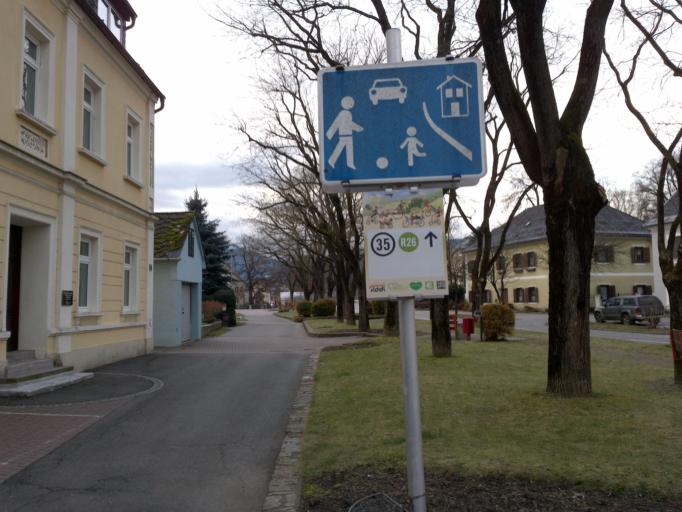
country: AT
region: Styria
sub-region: Politischer Bezirk Murtal
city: Weisskirchen in Steiermark
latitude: 47.1532
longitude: 14.7389
